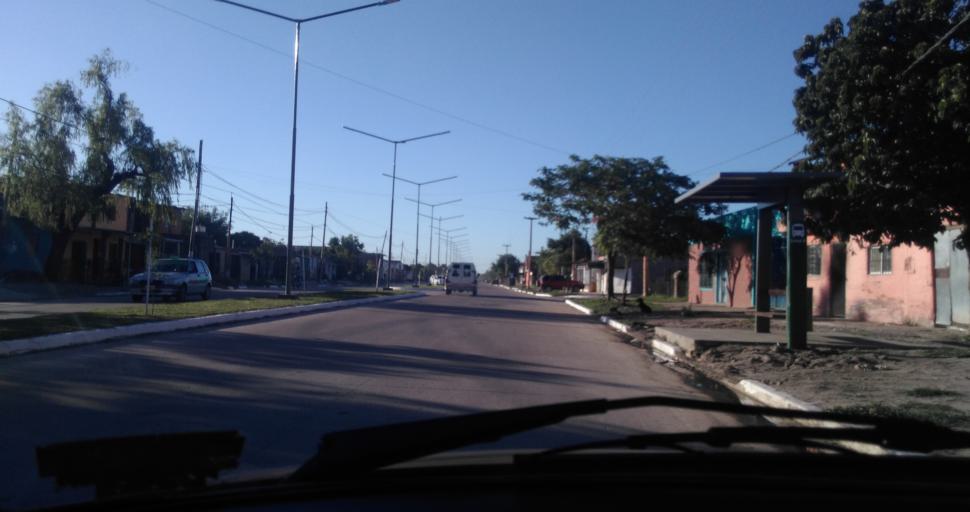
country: AR
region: Chaco
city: Resistencia
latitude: -27.4815
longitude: -58.9809
